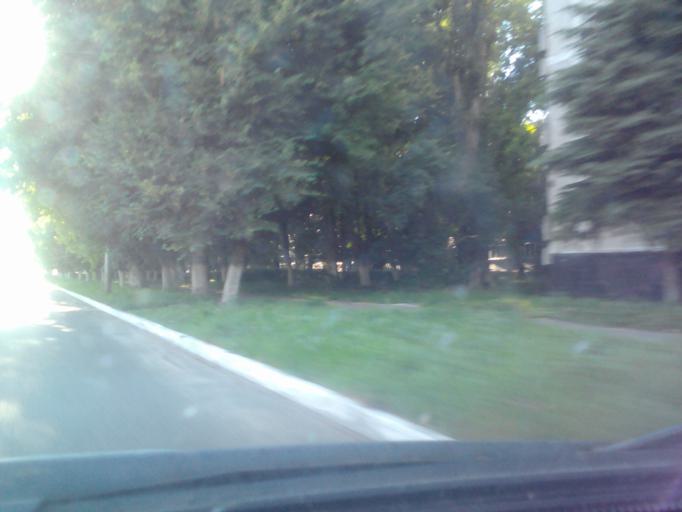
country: RU
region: Kursk
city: Kurchatov
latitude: 51.6590
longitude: 35.6477
